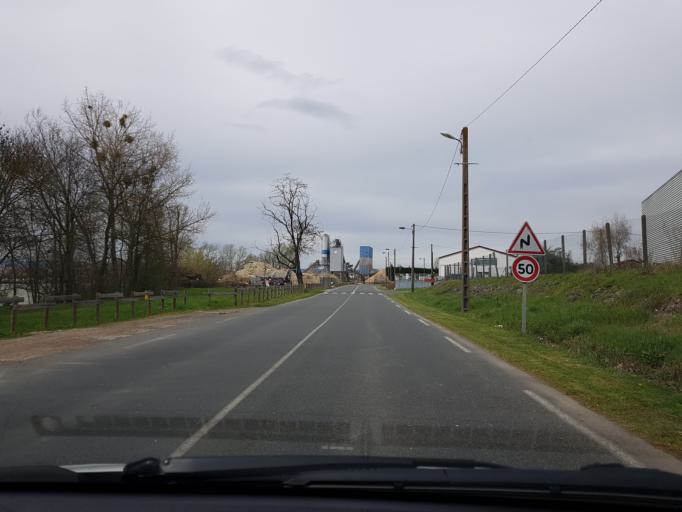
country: FR
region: Rhone-Alpes
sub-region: Departement de l'Ain
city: Jassans-Riottier
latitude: 45.9808
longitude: 4.7539
